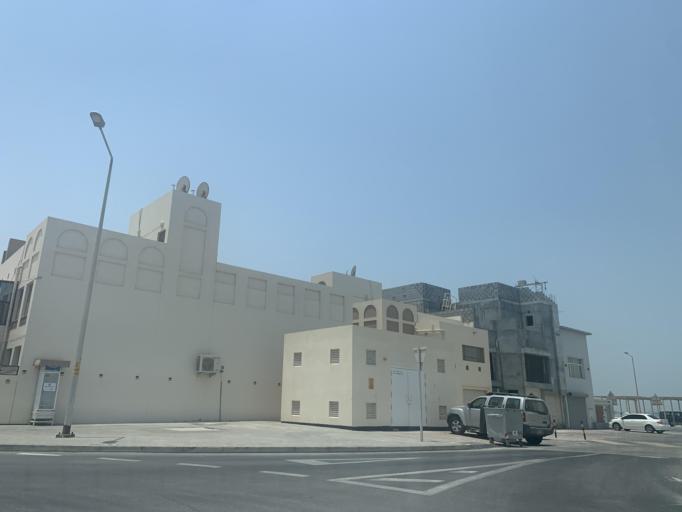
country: BH
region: Muharraq
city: Al Hadd
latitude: 26.2346
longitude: 50.6794
